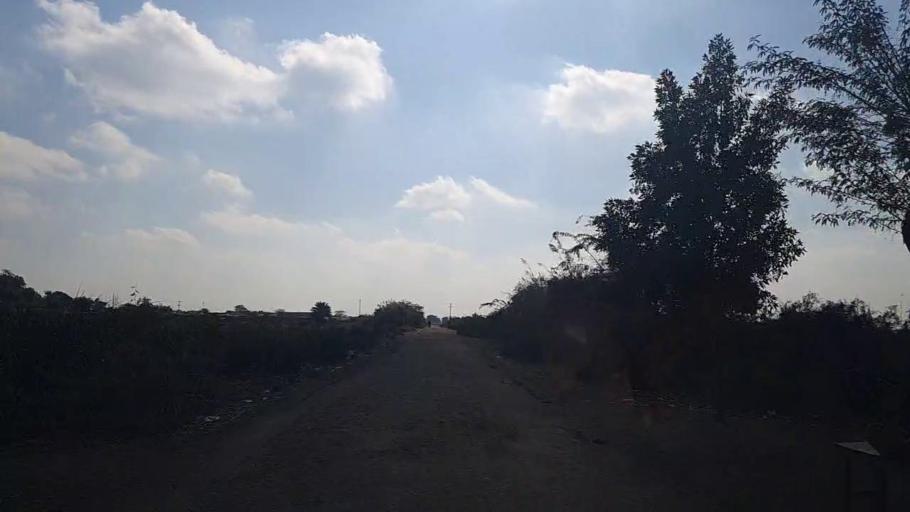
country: PK
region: Sindh
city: Sanghar
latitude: 26.0623
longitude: 69.0273
